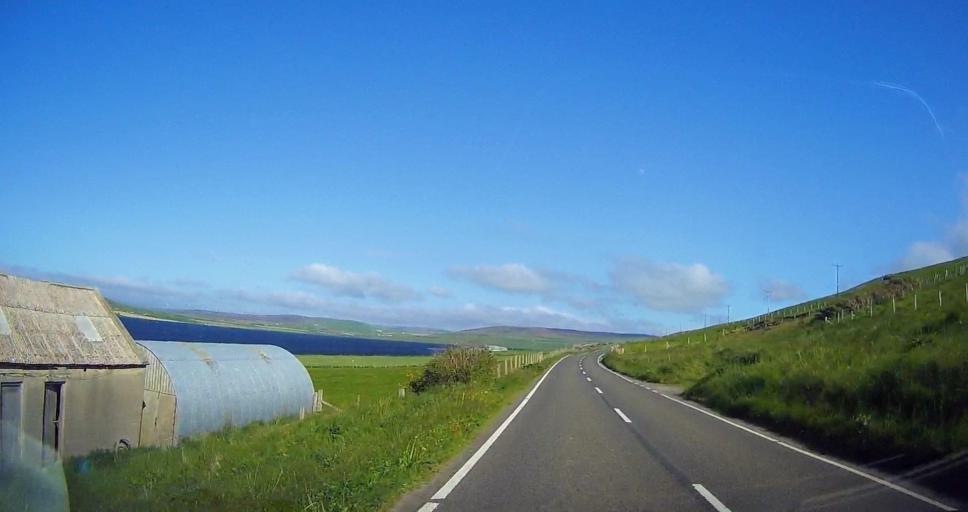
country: GB
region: Scotland
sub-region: Orkney Islands
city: Stromness
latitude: 59.1129
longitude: -3.2952
